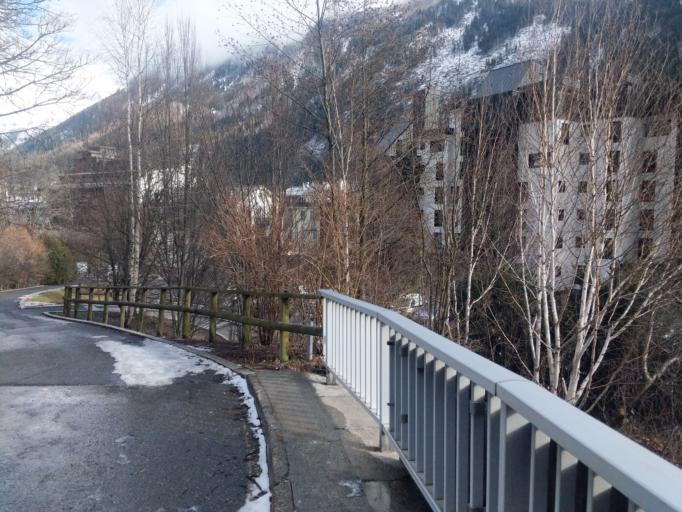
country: FR
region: Rhone-Alpes
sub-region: Departement de la Haute-Savoie
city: Chamonix-Mont-Blanc
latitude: 45.9225
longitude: 6.8673
